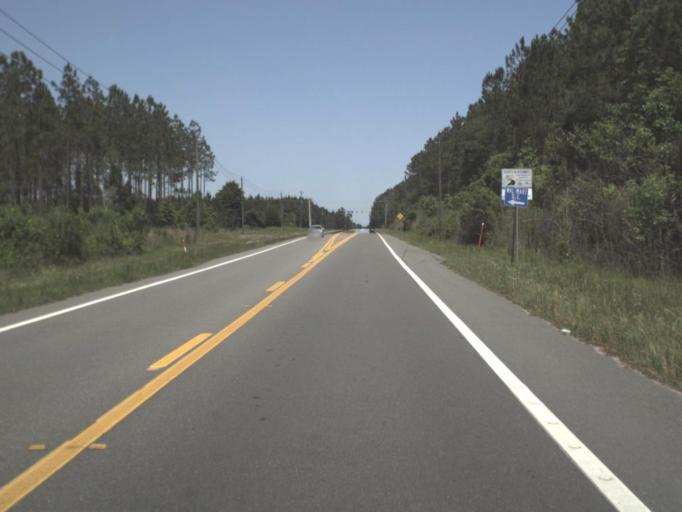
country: US
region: Florida
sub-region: Baker County
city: Macclenny
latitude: 30.2886
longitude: -82.0849
